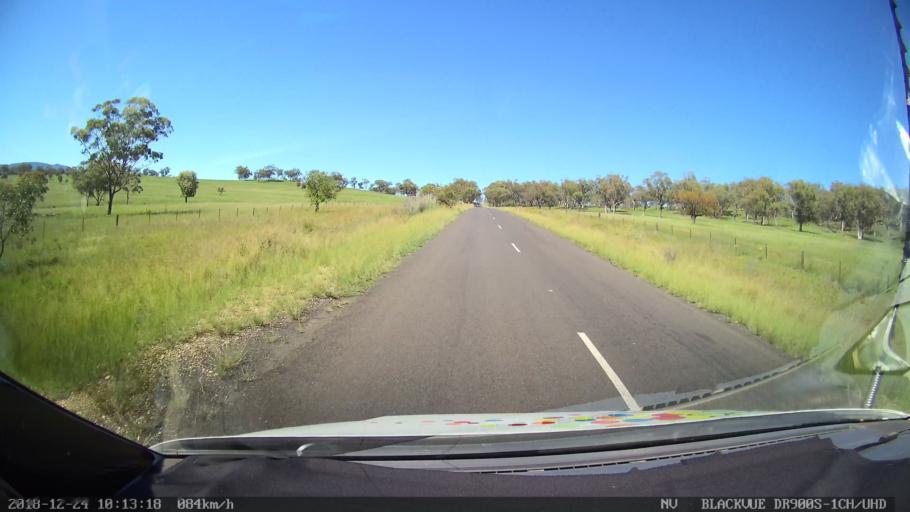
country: AU
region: New South Wales
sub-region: Liverpool Plains
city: Quirindi
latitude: -31.6884
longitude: 150.6407
